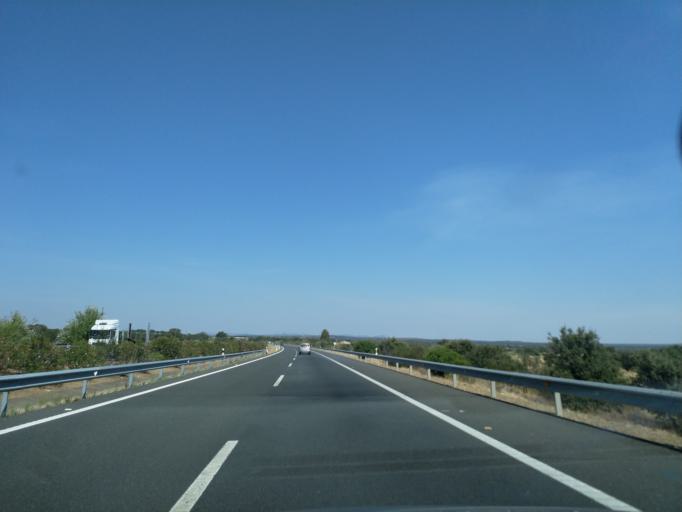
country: ES
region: Extremadura
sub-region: Provincia de Caceres
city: Casas de Don Antonio
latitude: 39.1907
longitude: -6.2769
